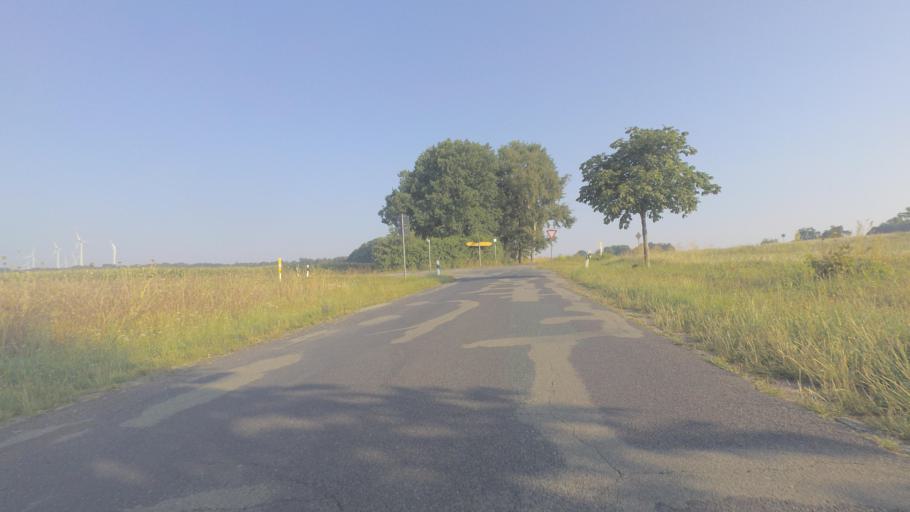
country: DE
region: Brandenburg
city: Heiligengrabe
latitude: 53.2624
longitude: 12.3335
